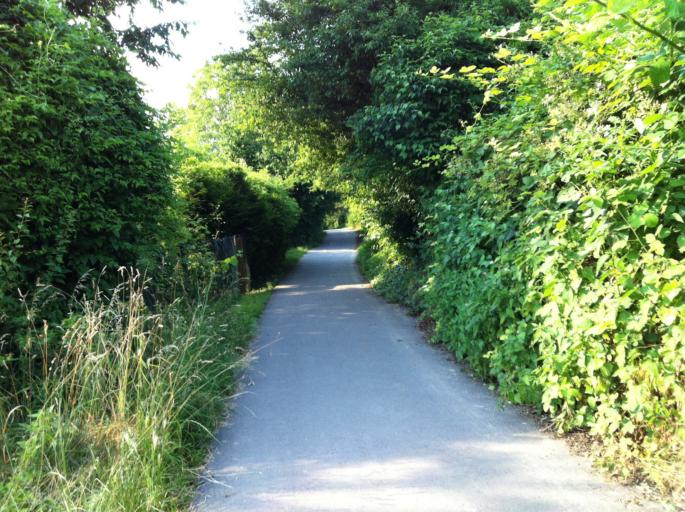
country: DE
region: Baden-Wuerttemberg
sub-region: Karlsruhe Region
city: Leimen
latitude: 49.3738
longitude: 8.6944
